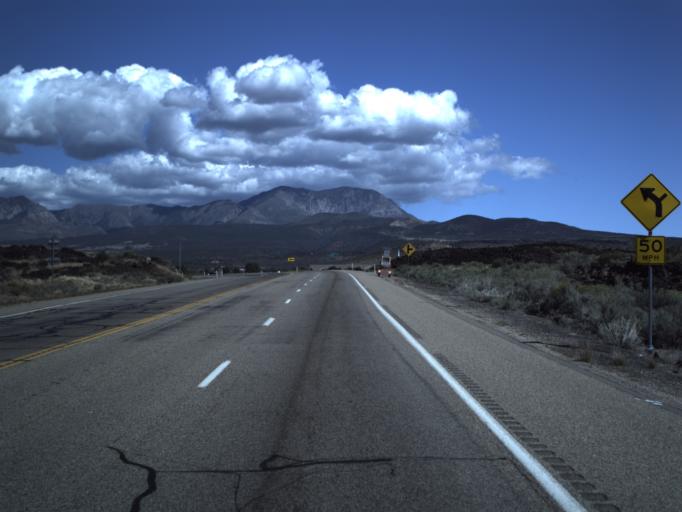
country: US
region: Utah
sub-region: Washington County
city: Ivins
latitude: 37.2459
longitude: -113.6295
